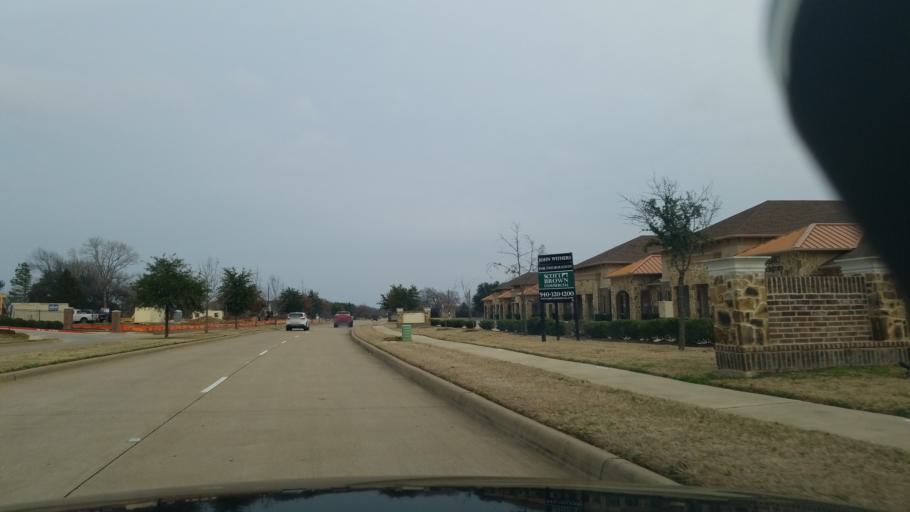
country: US
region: Texas
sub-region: Denton County
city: Corinth
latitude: 33.1532
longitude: -97.0554
